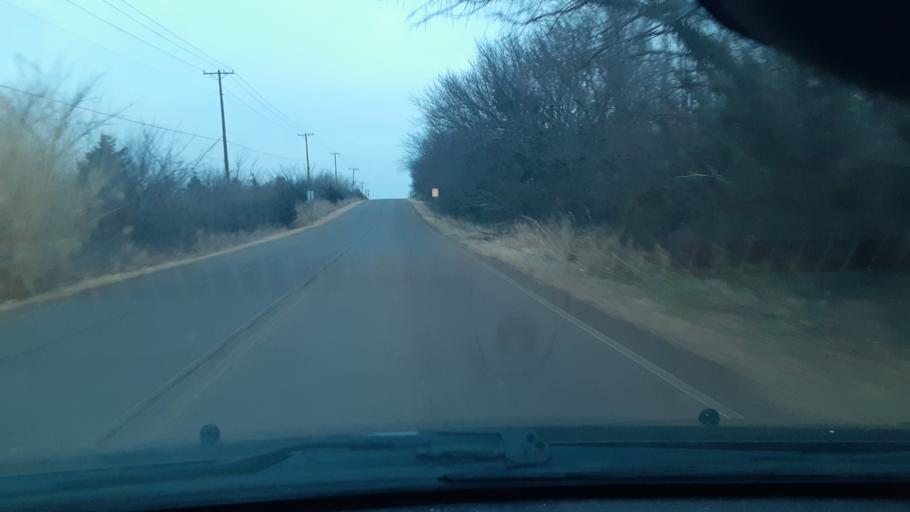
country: US
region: Oklahoma
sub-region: Logan County
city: Guthrie
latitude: 35.8607
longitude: -97.4075
